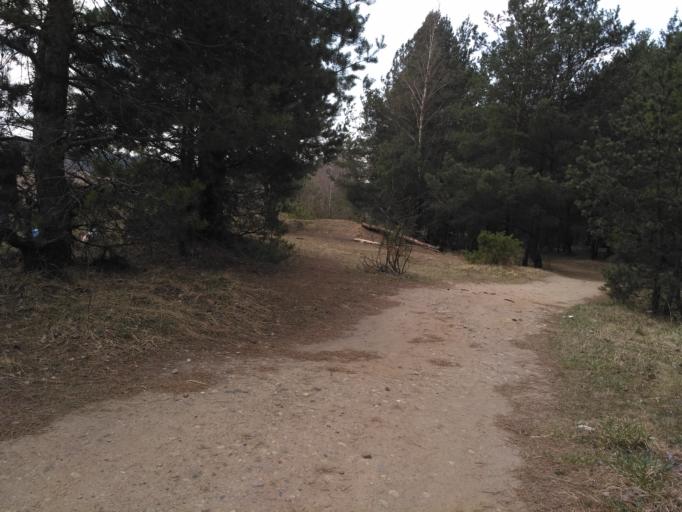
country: BY
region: Minsk
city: Zamostochcha
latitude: 53.8795
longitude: 27.9105
